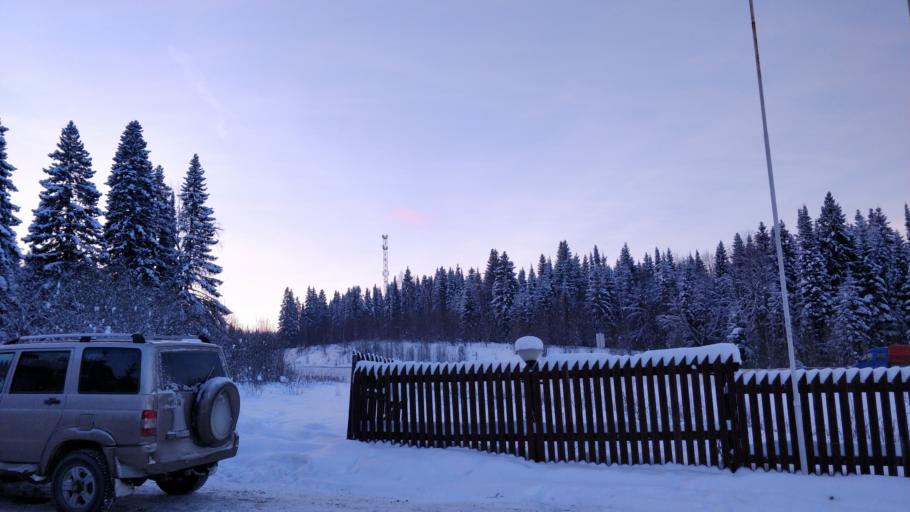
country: RU
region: Perm
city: Sylva
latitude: 58.2935
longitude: 56.8396
